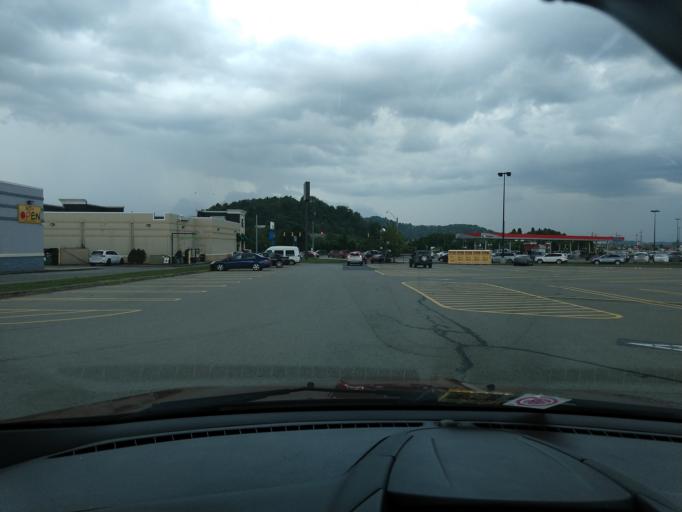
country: US
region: West Virginia
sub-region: Harrison County
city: Bridgeport
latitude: 39.2756
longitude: -80.2811
